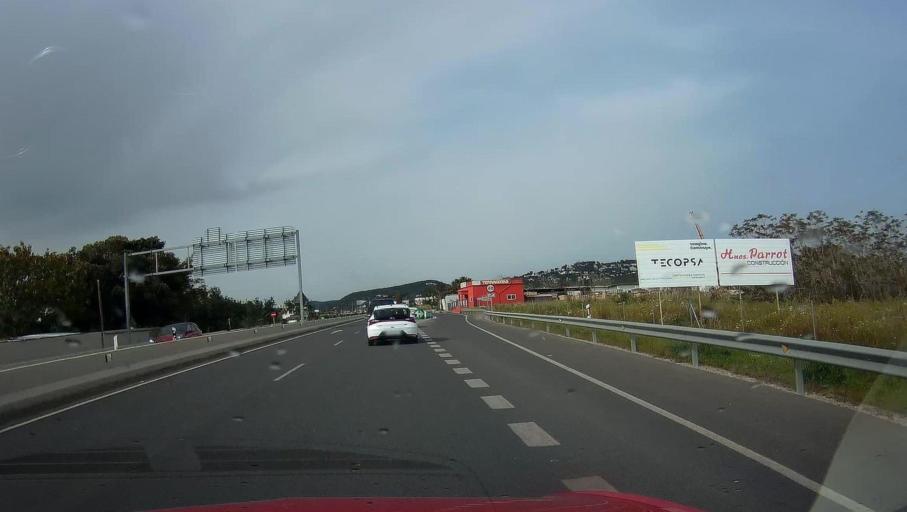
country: ES
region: Balearic Islands
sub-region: Illes Balears
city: Ibiza
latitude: 38.9311
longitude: 1.4434
